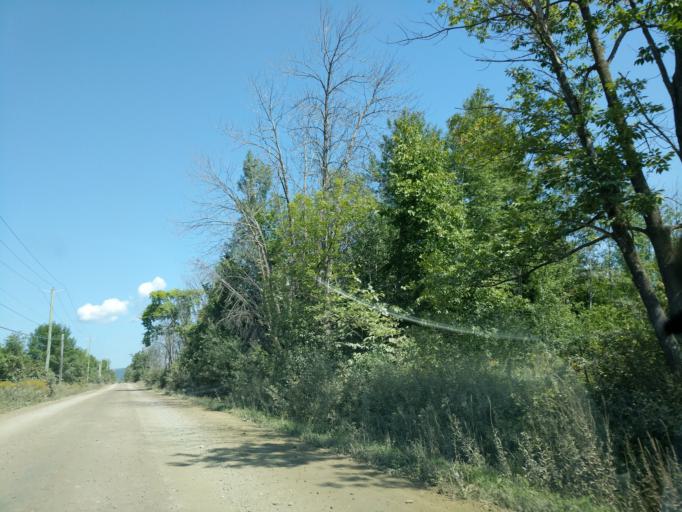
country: CA
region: Ontario
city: Bells Corners
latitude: 45.4375
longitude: -75.9015
